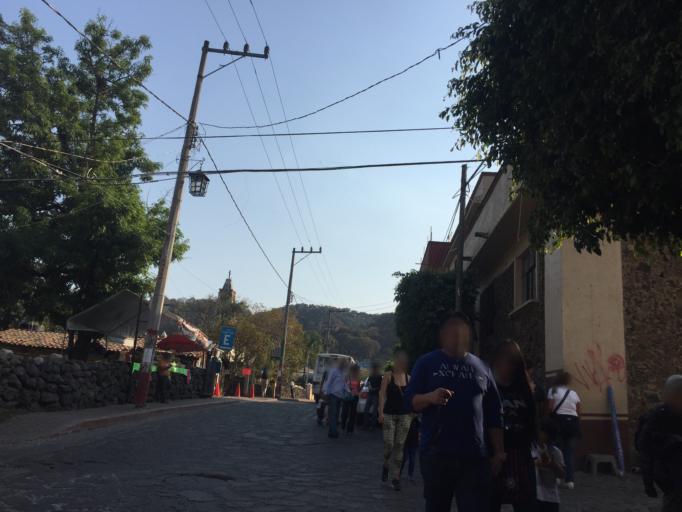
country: MX
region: Morelos
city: Tepoztlan
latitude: 18.9839
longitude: -99.1019
